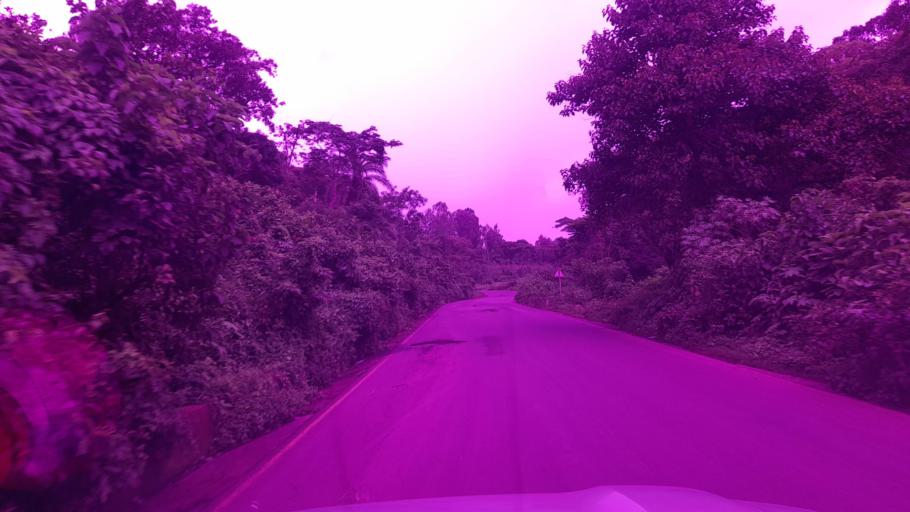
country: ET
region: Oromiya
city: Jima
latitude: 7.6617
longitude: 36.8852
